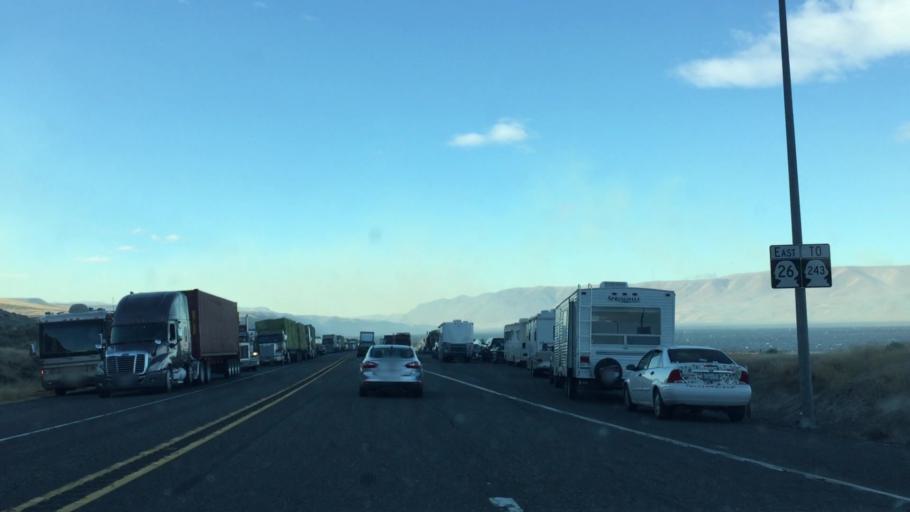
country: US
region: Washington
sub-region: Grant County
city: Mattawa
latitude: 46.9404
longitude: -119.9612
